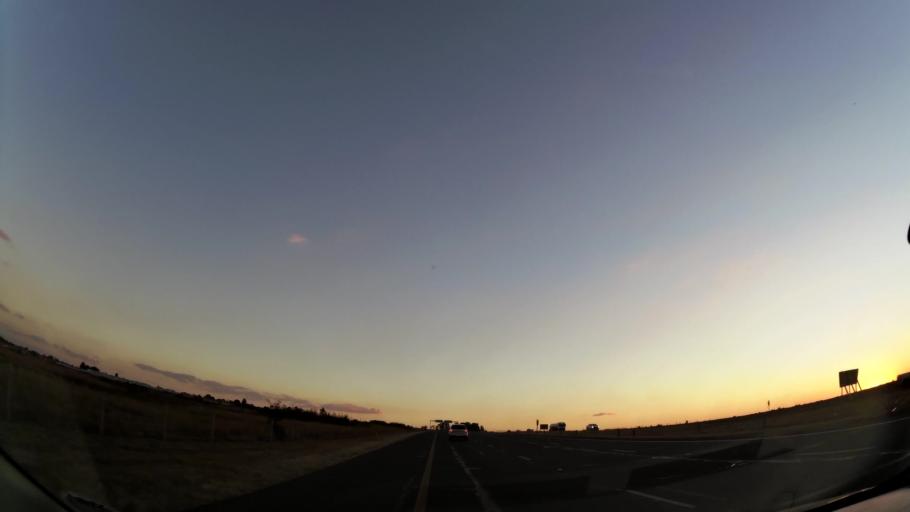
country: ZA
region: Mpumalanga
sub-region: Nkangala District Municipality
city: Witbank
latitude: -25.8932
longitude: 29.2626
